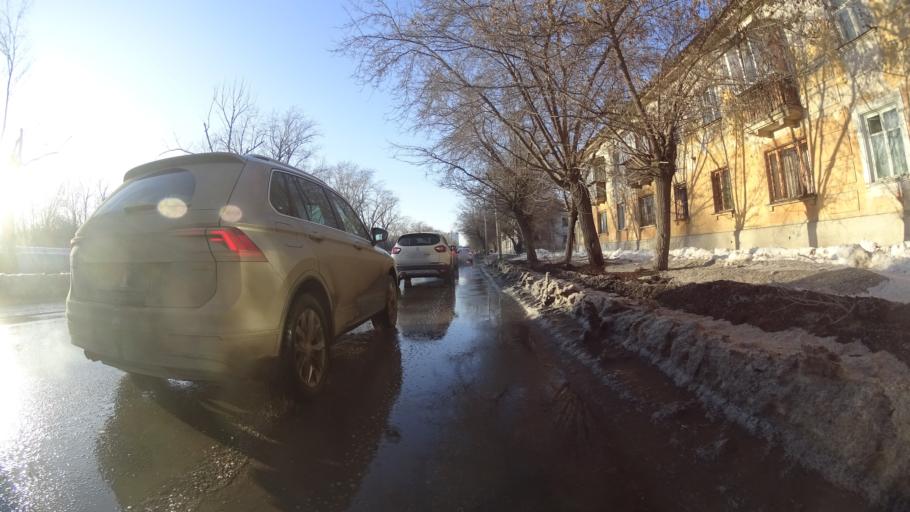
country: RU
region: Chelyabinsk
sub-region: Gorod Chelyabinsk
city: Chelyabinsk
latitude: 55.1329
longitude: 61.4611
